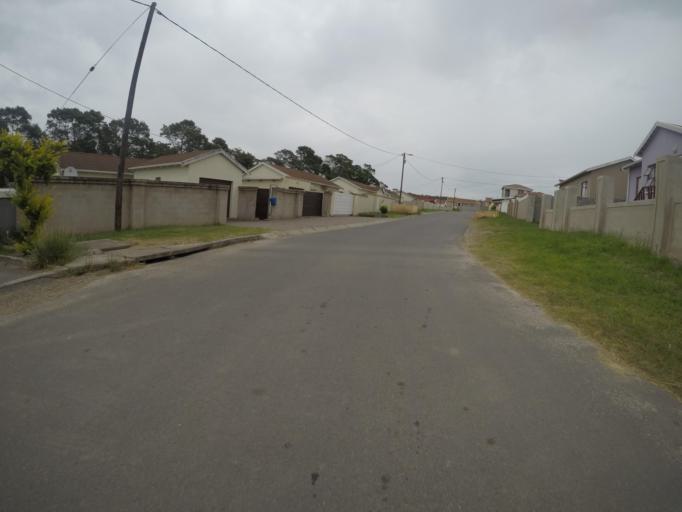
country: ZA
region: Eastern Cape
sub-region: Buffalo City Metropolitan Municipality
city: East London
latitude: -32.9945
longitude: 27.8441
